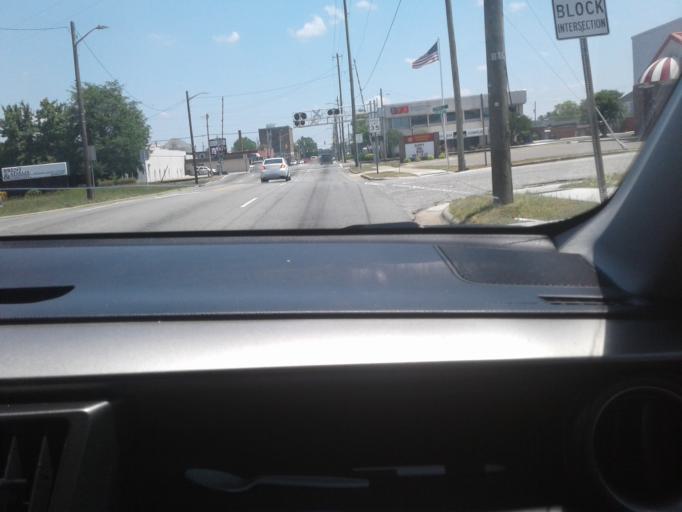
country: US
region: North Carolina
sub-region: Harnett County
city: Dunn
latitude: 35.3078
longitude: -78.6119
